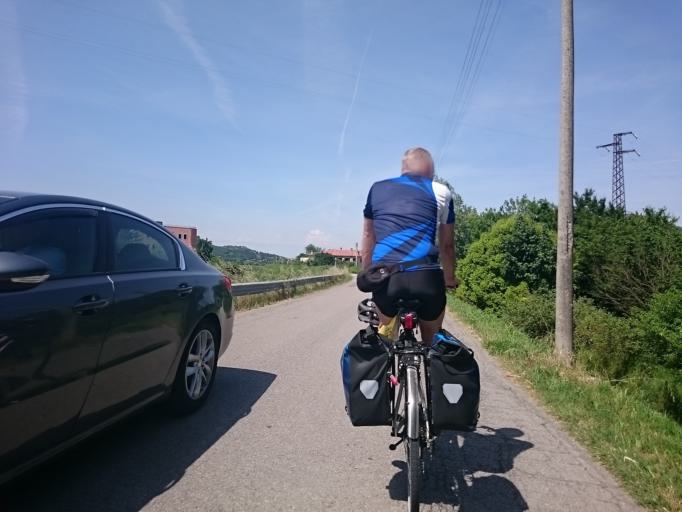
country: IT
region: Veneto
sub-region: Provincia di Padova
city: Vo
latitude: 45.3268
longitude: 11.6181
